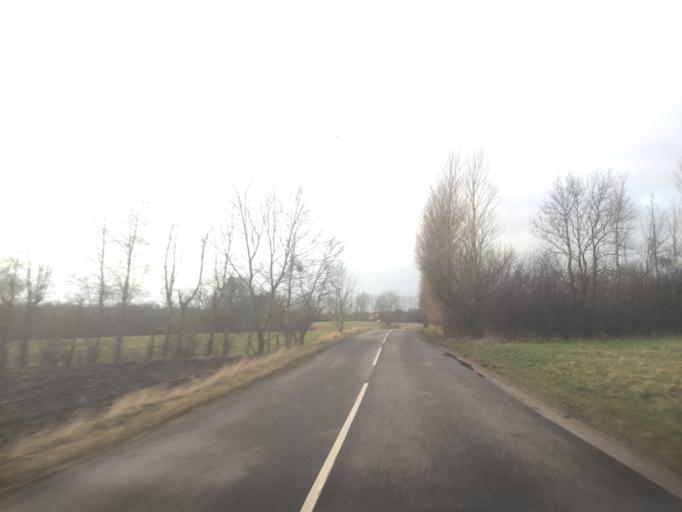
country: DK
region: Capital Region
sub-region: Egedal Kommune
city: Smorumnedre
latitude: 55.7159
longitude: 12.2776
